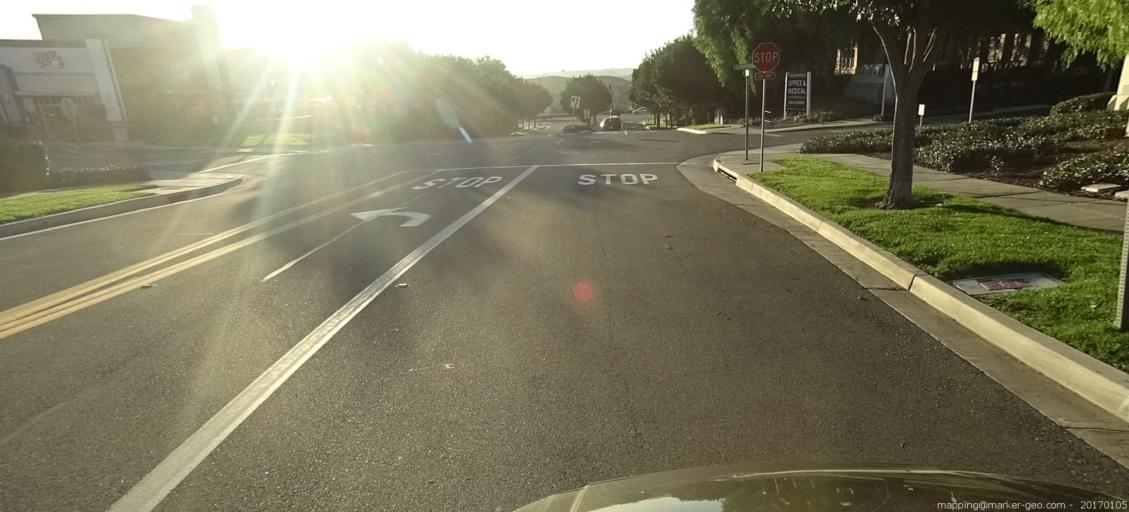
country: US
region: California
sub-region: Orange County
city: Ladera Ranch
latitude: 33.5562
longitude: -117.6287
